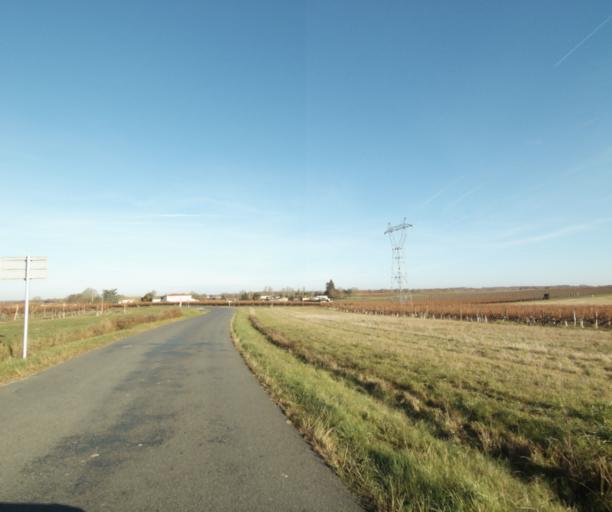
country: FR
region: Poitou-Charentes
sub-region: Departement de la Charente-Maritime
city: Cherac
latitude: 45.7391
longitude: -0.4498
